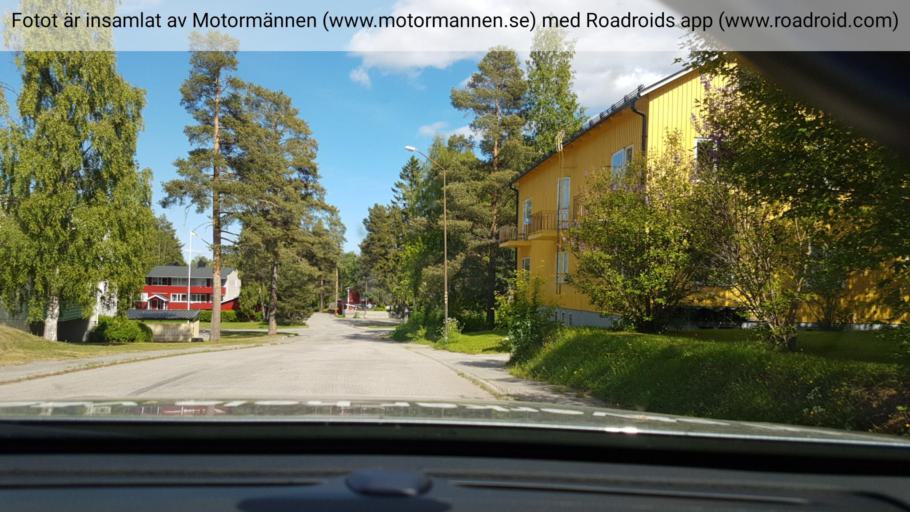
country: SE
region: Vaesterbotten
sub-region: Lycksele Kommun
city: Lycksele
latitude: 64.5932
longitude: 18.6652
